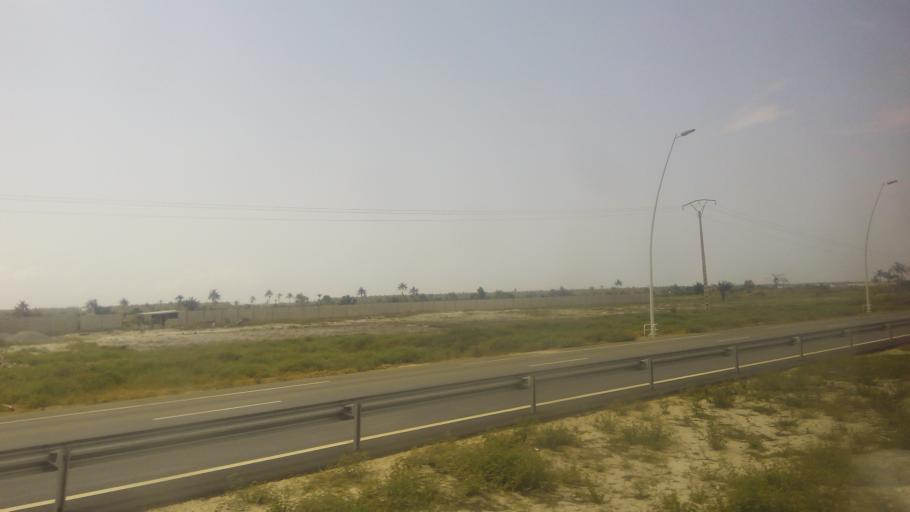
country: CI
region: Sud-Comoe
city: Grand-Bassam
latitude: 5.2353
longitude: -3.7951
